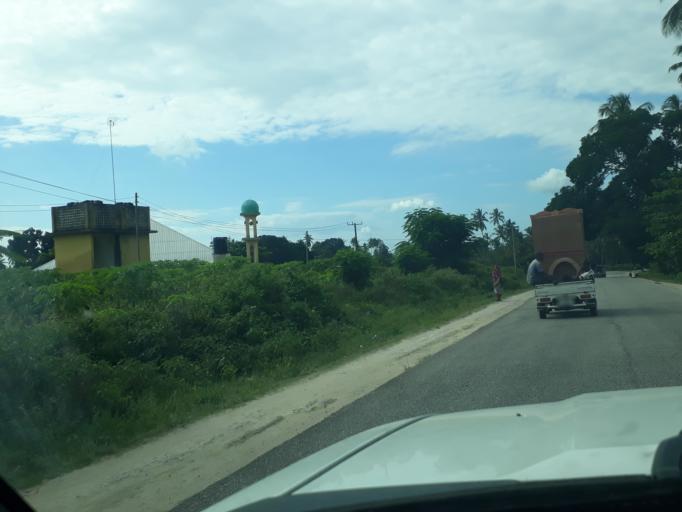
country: TZ
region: Zanzibar North
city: Mkokotoni
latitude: -5.8815
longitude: 39.2545
